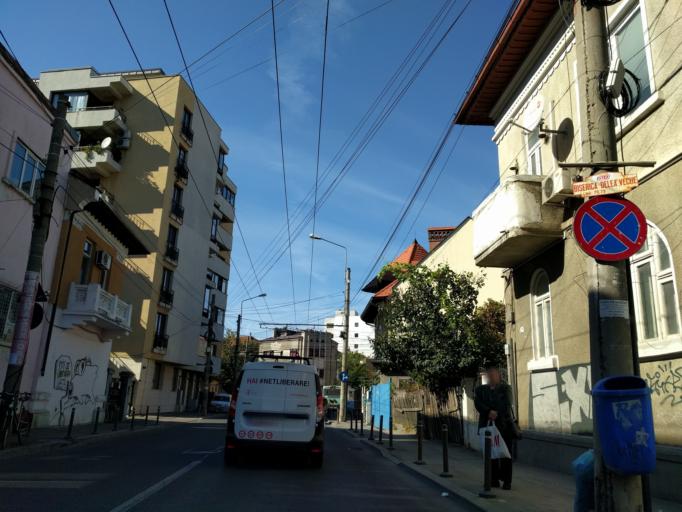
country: RO
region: Bucuresti
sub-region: Municipiul Bucuresti
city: Bucharest
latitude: 44.4339
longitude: 26.1274
